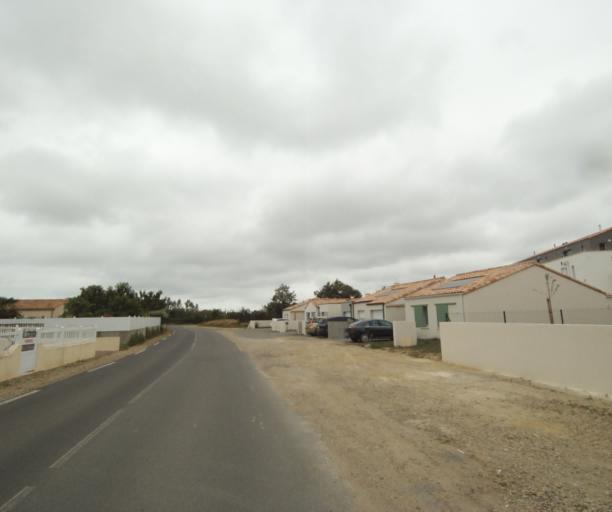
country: FR
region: Pays de la Loire
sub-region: Departement de la Vendee
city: Chateau-d'Olonne
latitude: 46.5076
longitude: -1.7472
